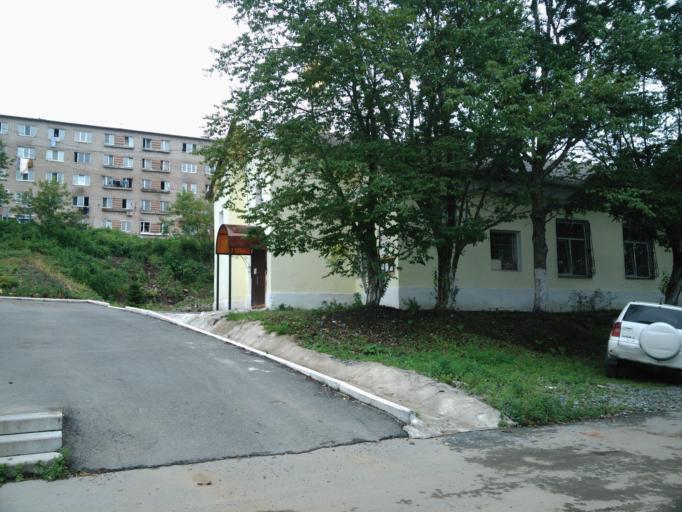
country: RU
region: Primorskiy
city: Vladivostok
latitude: 43.0917
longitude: 131.9590
